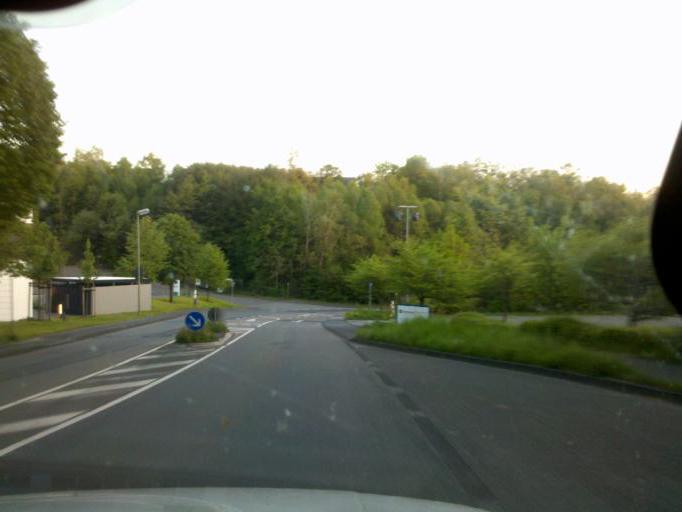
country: DE
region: North Rhine-Westphalia
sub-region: Regierungsbezirk Koln
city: Gummersbach
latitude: 51.0123
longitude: 7.5601
